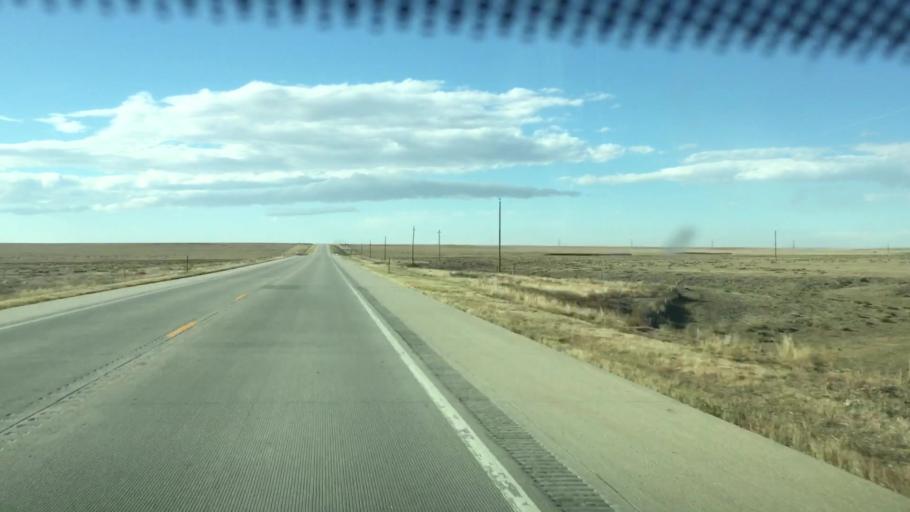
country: US
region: Colorado
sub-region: Lincoln County
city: Hugo
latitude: 39.0674
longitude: -103.3707
